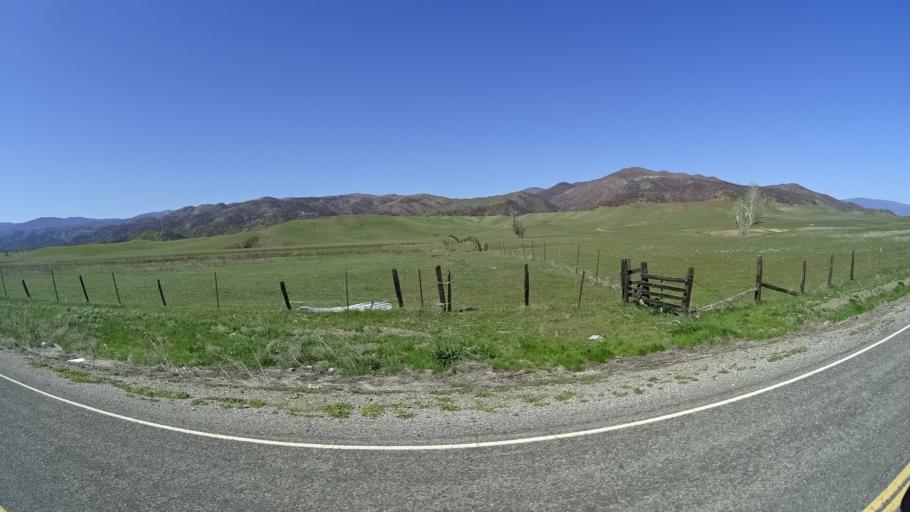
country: US
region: California
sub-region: Tehama County
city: Rancho Tehama Reserve
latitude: 39.7149
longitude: -122.5484
